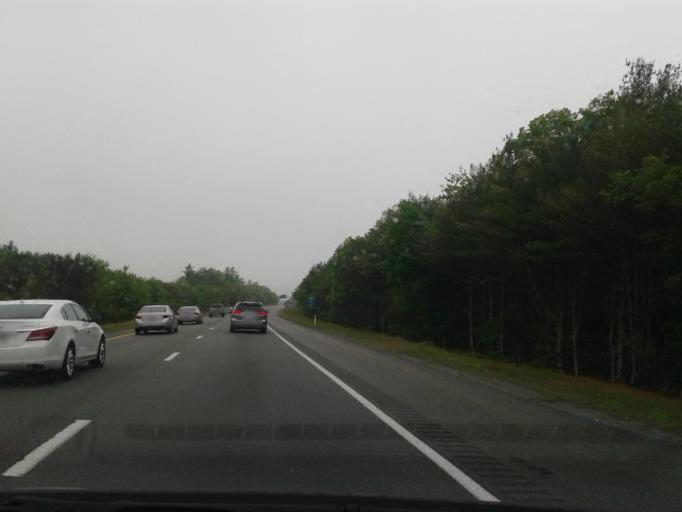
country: US
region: Massachusetts
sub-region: Plymouth County
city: Mattapoisett Center
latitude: 41.6875
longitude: -70.8084
